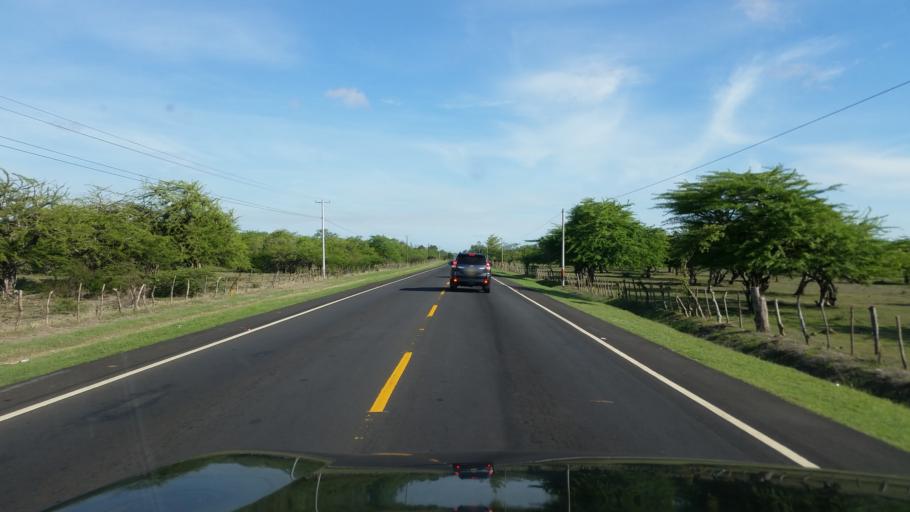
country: NI
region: Leon
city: La Paz Centro
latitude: 12.2749
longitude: -86.7443
